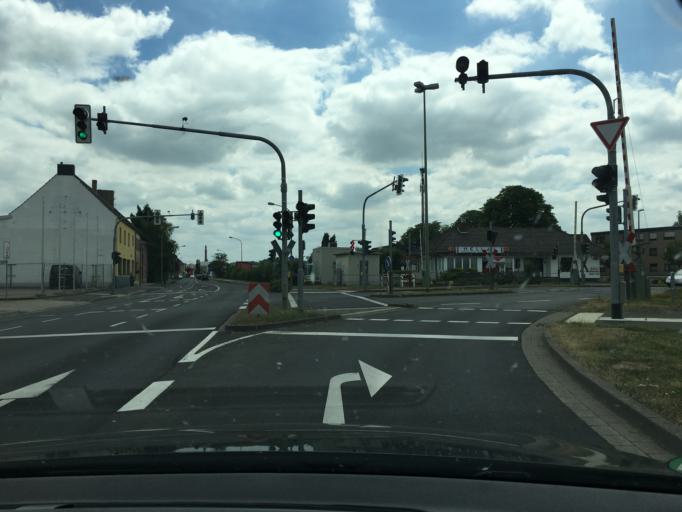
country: DE
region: North Rhine-Westphalia
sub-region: Regierungsbezirk Koln
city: Kreuzau
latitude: 50.7518
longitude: 6.4879
